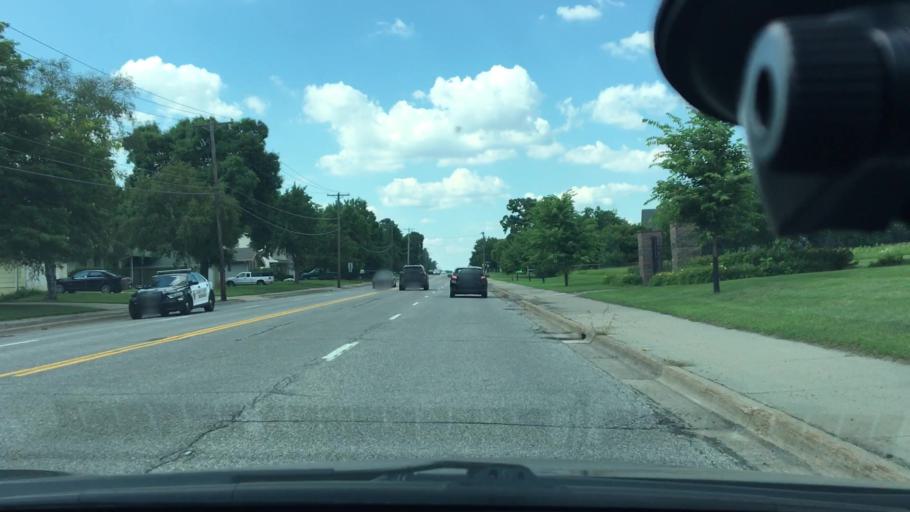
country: US
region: Minnesota
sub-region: Hennepin County
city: New Hope
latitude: 45.0260
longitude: -93.3802
